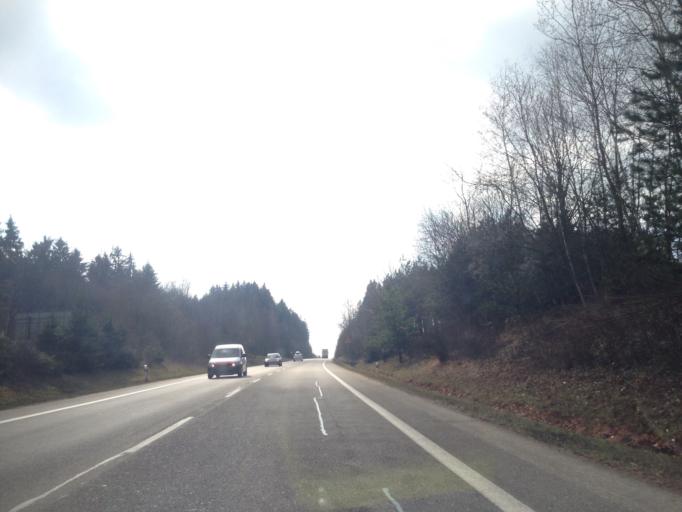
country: CZ
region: Kralovehradecky
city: Nova Paka
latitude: 50.4601
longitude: 15.4885
